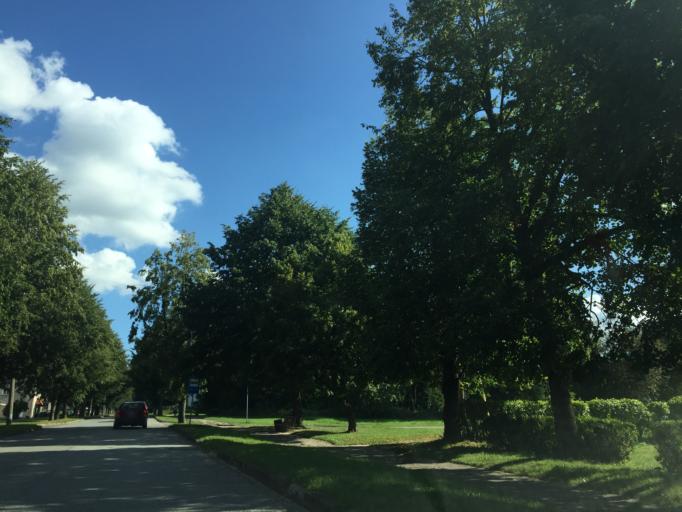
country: LV
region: Priekuli
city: Priekuli
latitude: 57.3866
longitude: 25.4224
